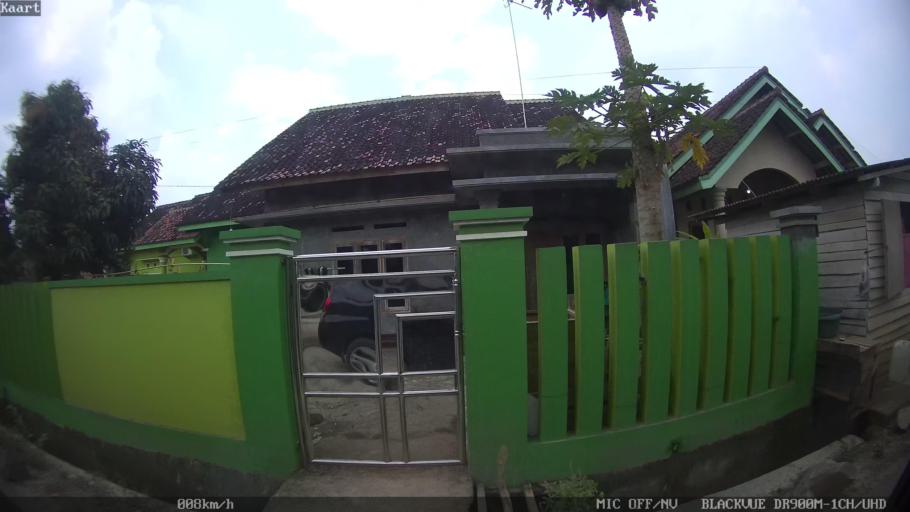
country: ID
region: Lampung
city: Gadingrejo
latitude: -5.3798
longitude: 105.0340
